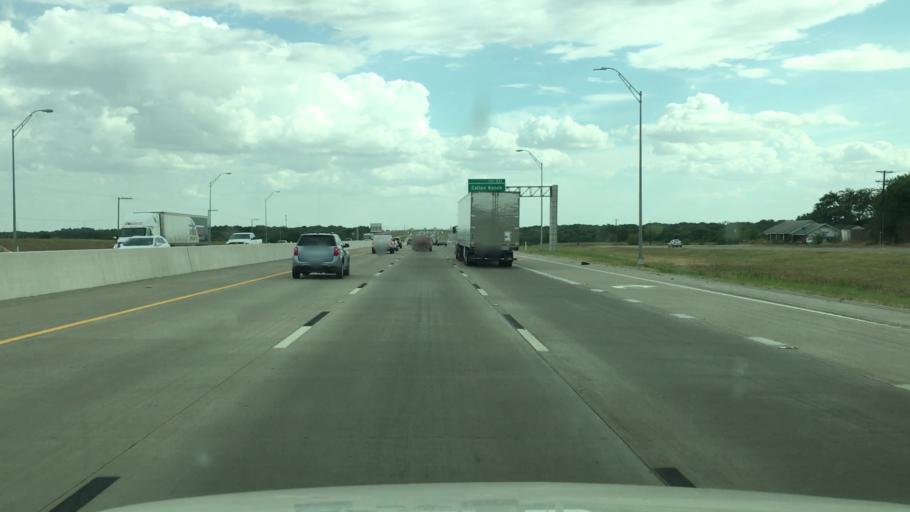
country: US
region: Texas
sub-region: McLennan County
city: Lorena
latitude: 31.3772
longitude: -97.2145
